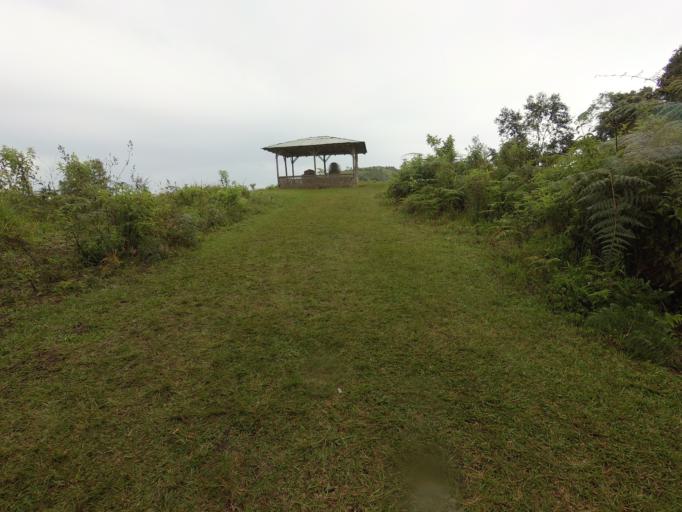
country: CO
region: Huila
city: San Agustin
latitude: 1.9126
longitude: -76.2937
